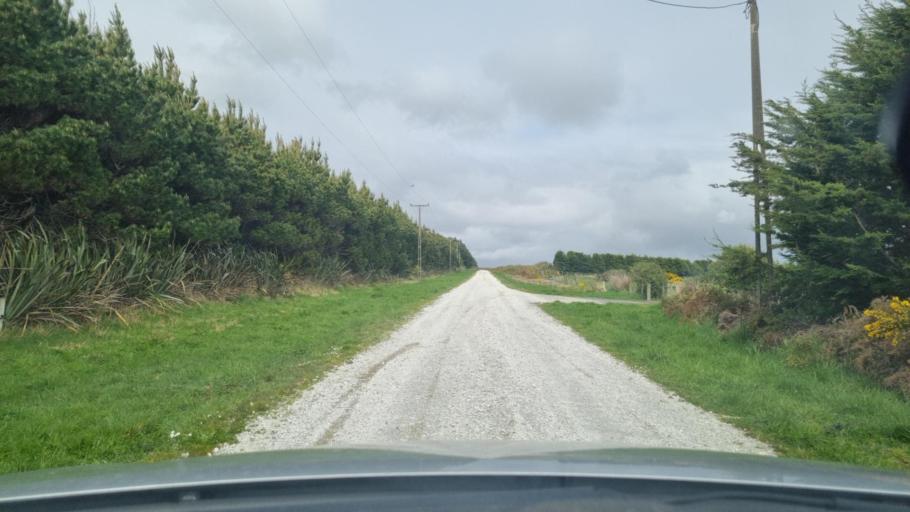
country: NZ
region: Southland
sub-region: Invercargill City
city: Bluff
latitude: -46.5128
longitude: 168.3543
